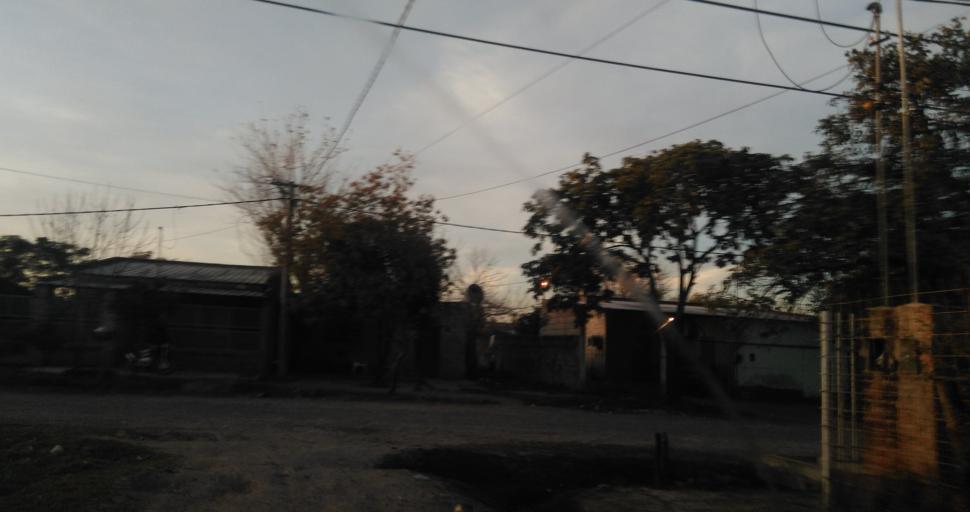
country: AR
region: Chaco
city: Resistencia
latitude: -27.4802
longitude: -58.9943
